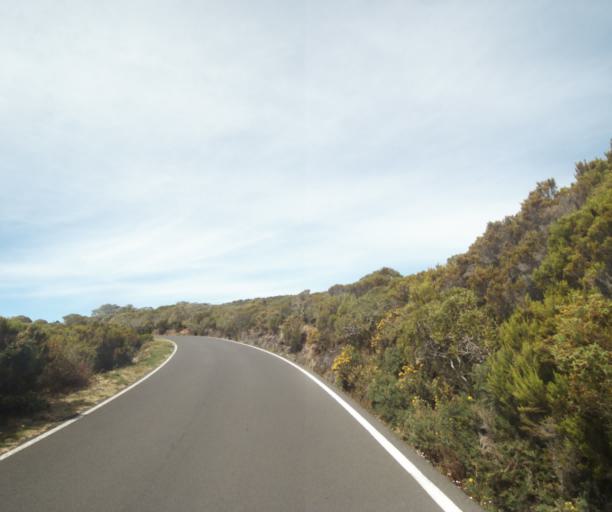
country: RE
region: Reunion
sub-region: Reunion
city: Trois-Bassins
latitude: -21.0718
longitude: 55.3832
